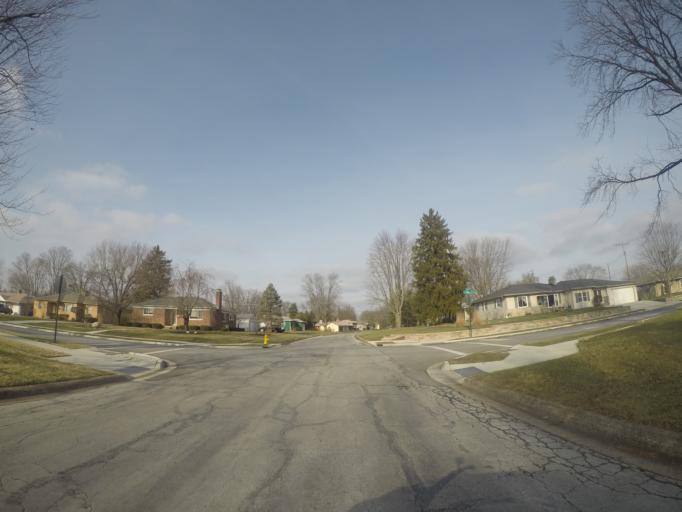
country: US
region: Ohio
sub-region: Franklin County
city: Upper Arlington
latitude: 40.0217
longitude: -83.0638
